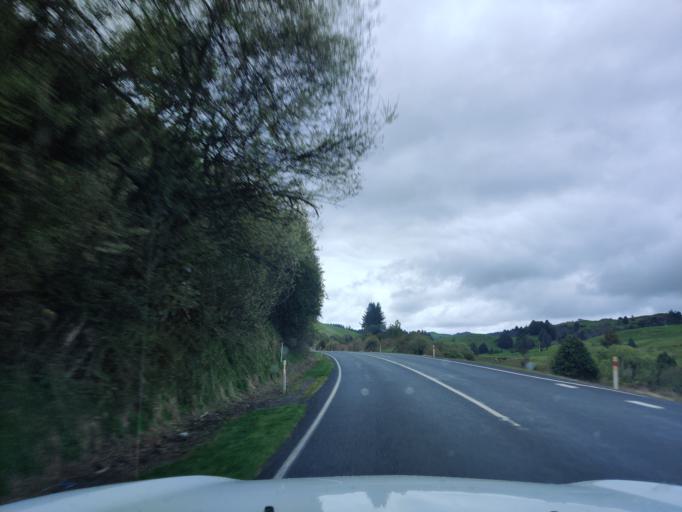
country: NZ
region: Waikato
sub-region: Otorohanga District
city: Otorohanga
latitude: -38.5931
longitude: 175.2195
